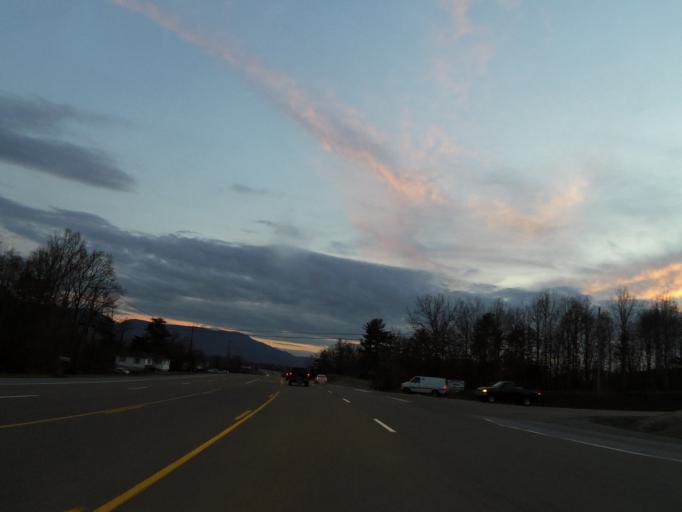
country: US
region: Tennessee
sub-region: McMinn County
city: Etowah
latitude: 35.2893
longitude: -84.5444
